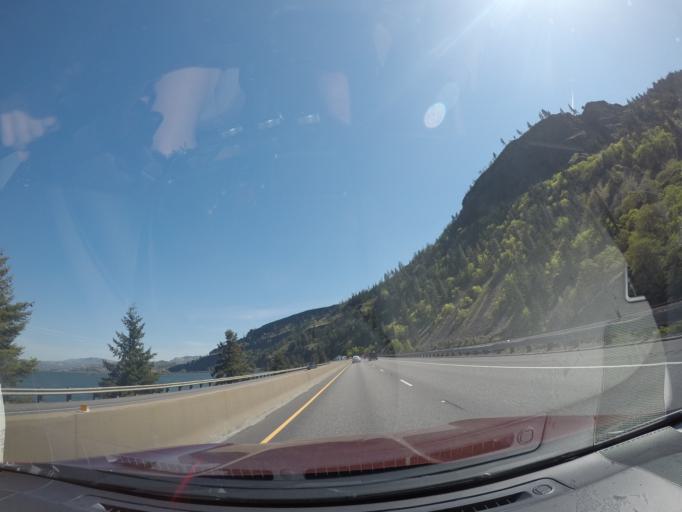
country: US
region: Washington
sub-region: Klickitat County
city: White Salmon
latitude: 45.6911
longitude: -121.4398
